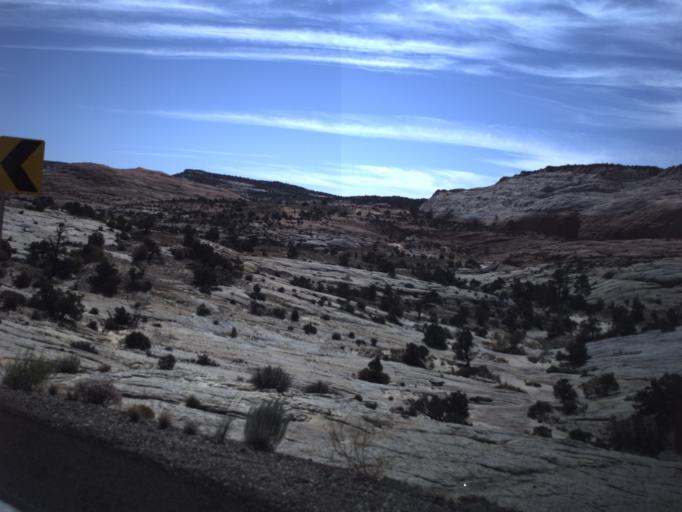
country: US
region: Utah
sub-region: Wayne County
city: Loa
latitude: 37.7496
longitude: -111.4440
